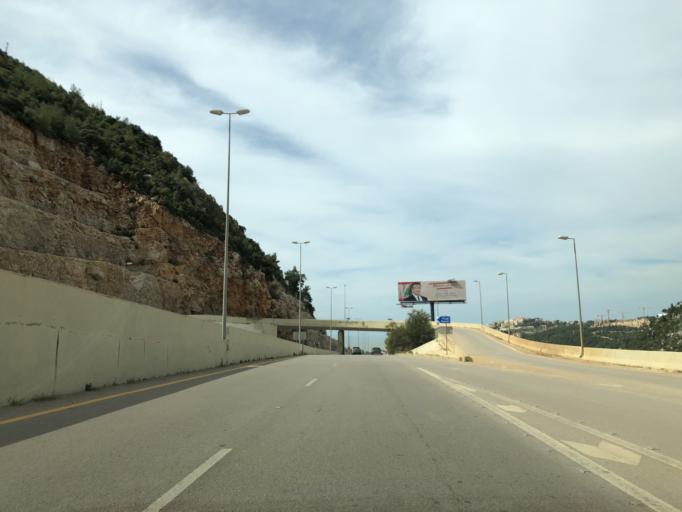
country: LB
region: Mont-Liban
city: Jdaidet el Matn
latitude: 33.8970
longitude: 35.6490
